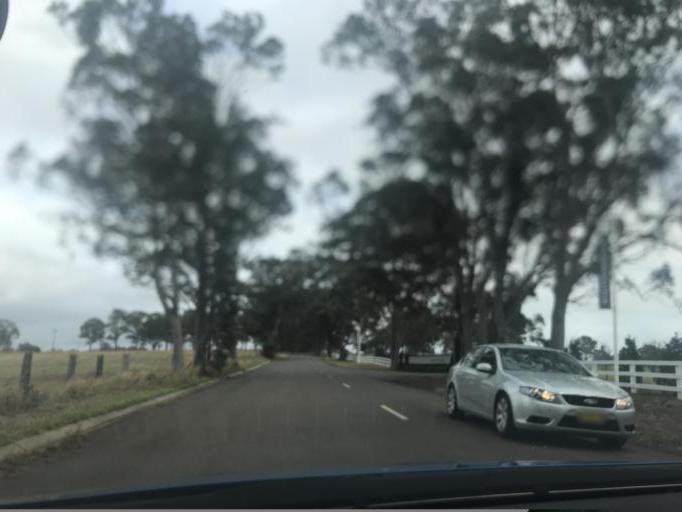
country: AU
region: New South Wales
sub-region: Cessnock
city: Cessnock
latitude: -32.8114
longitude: 151.3082
